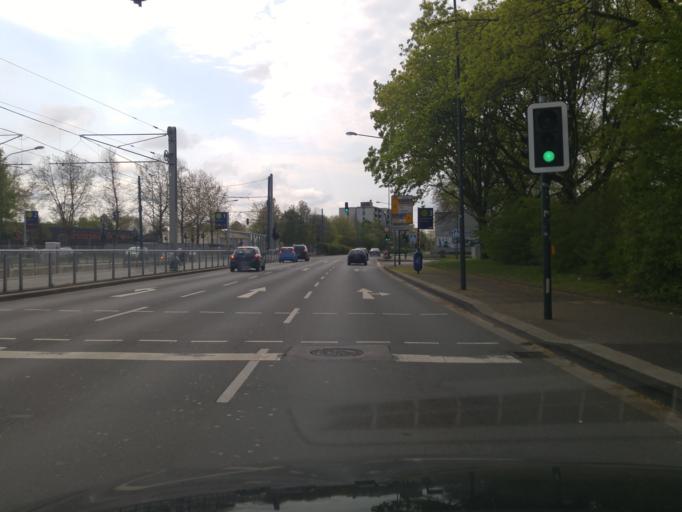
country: DE
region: North Rhine-Westphalia
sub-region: Regierungsbezirk Dusseldorf
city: Essen
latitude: 51.4708
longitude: 7.0176
